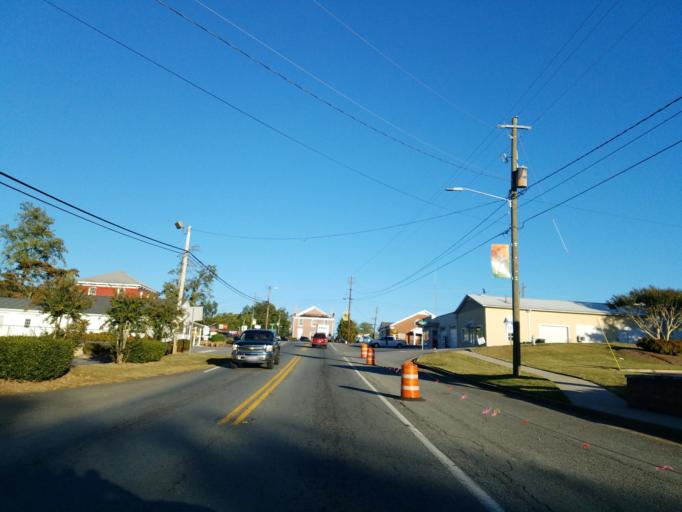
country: US
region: Georgia
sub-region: Dawson County
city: Dawsonville
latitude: 34.4213
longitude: -84.1208
